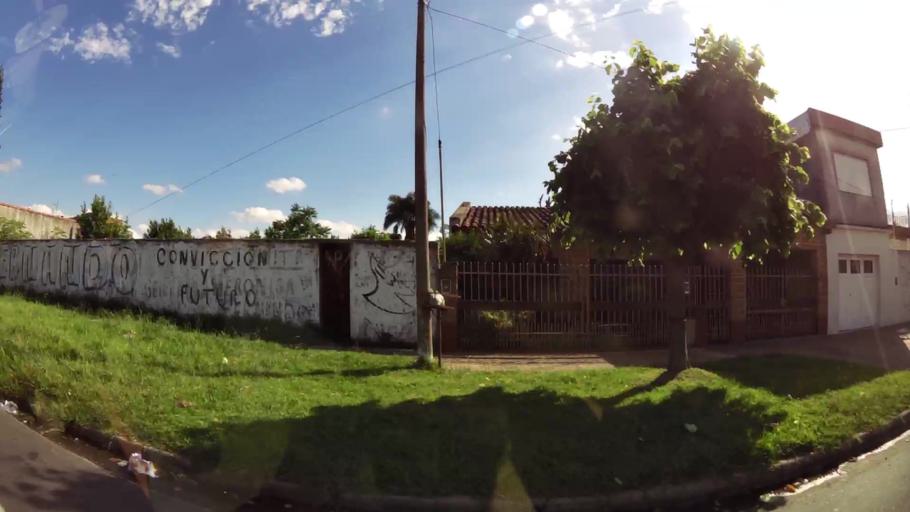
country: AR
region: Buenos Aires
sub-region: Partido de Moron
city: Moron
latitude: -34.6621
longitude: -58.5917
